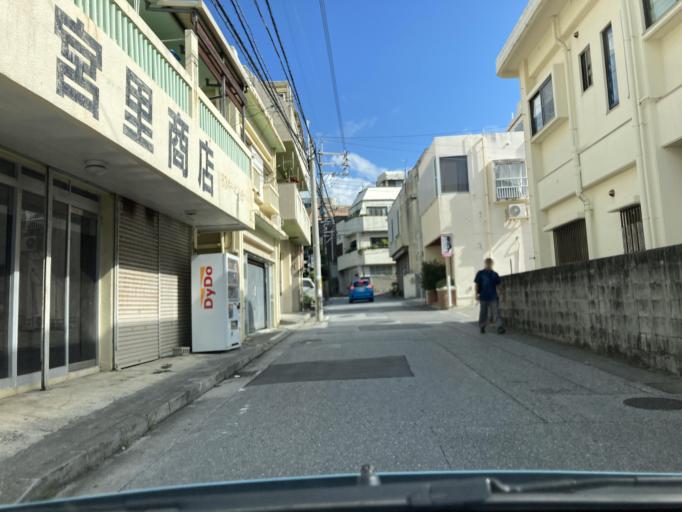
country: JP
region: Okinawa
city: Naha-shi
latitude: 26.2141
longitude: 127.7077
